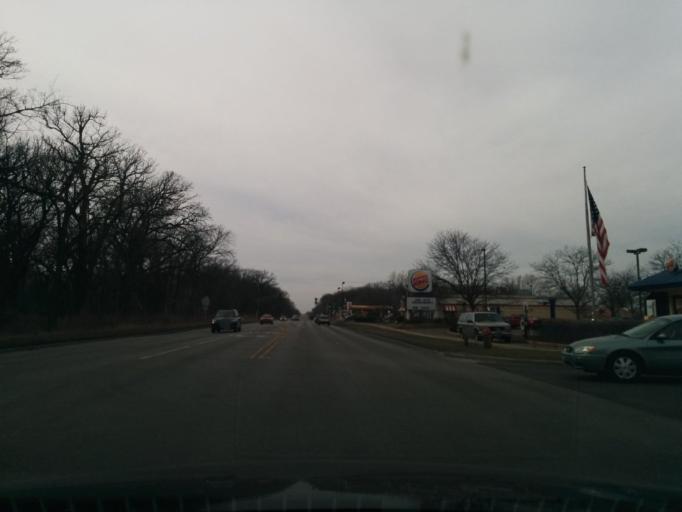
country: US
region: Illinois
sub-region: Cook County
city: Westchester
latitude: 41.8337
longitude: -87.8984
